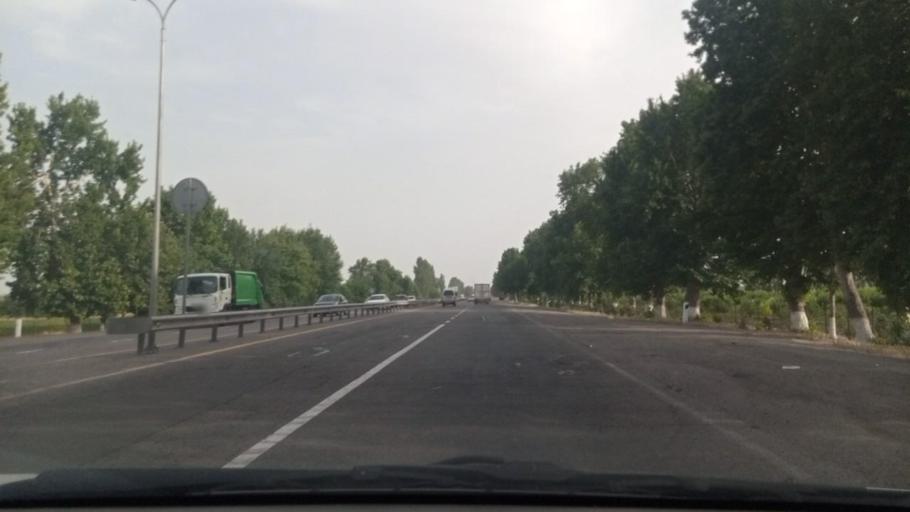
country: UZ
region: Toshkent Shahri
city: Bektemir
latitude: 41.2200
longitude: 69.4024
